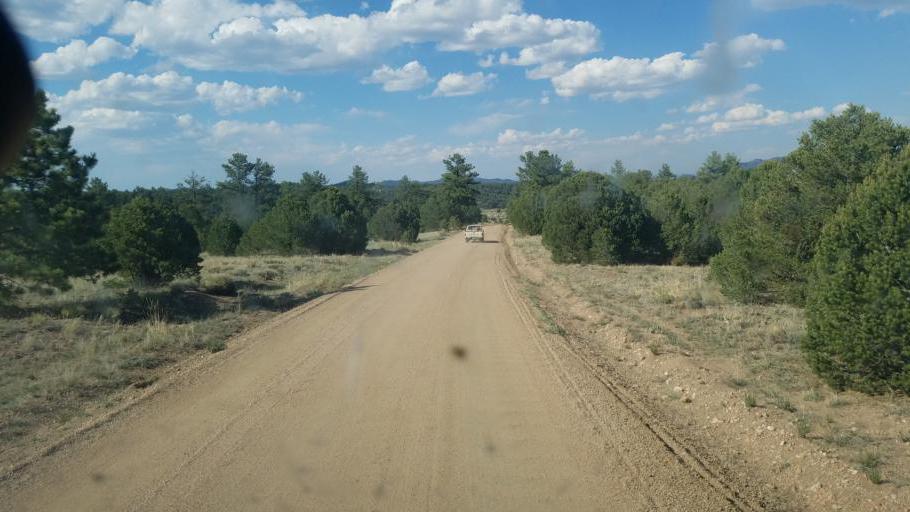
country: US
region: Colorado
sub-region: Custer County
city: Westcliffe
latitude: 38.2734
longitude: -105.4683
